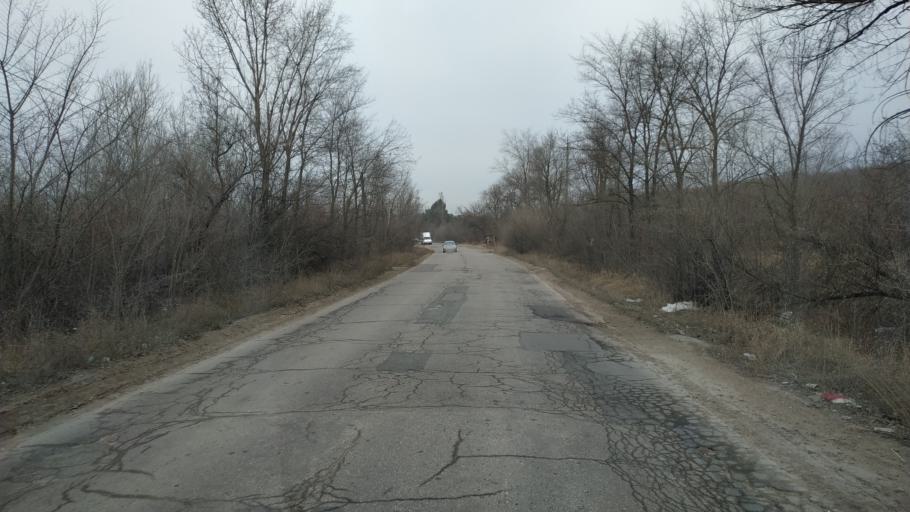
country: MD
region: Chisinau
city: Vatra
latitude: 47.0708
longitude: 28.7742
